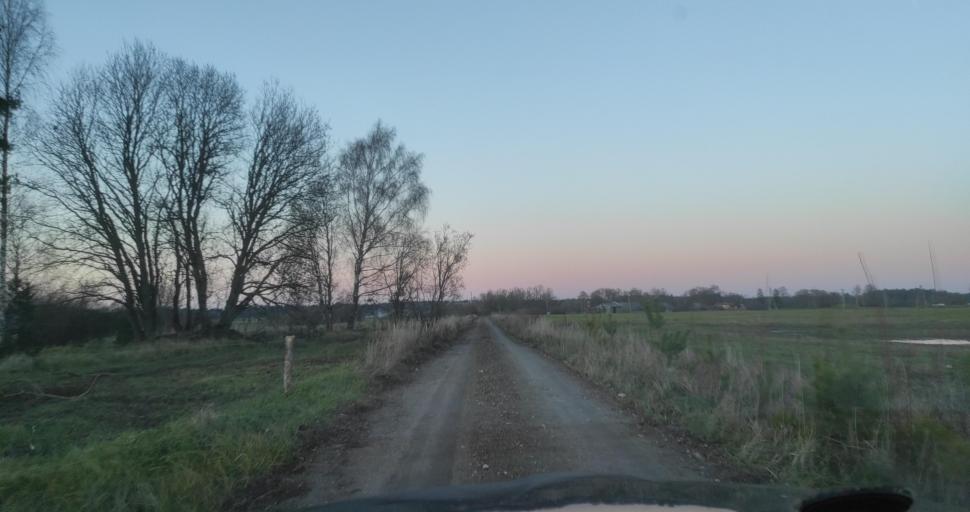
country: LV
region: Dundaga
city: Dundaga
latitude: 57.3713
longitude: 22.2243
